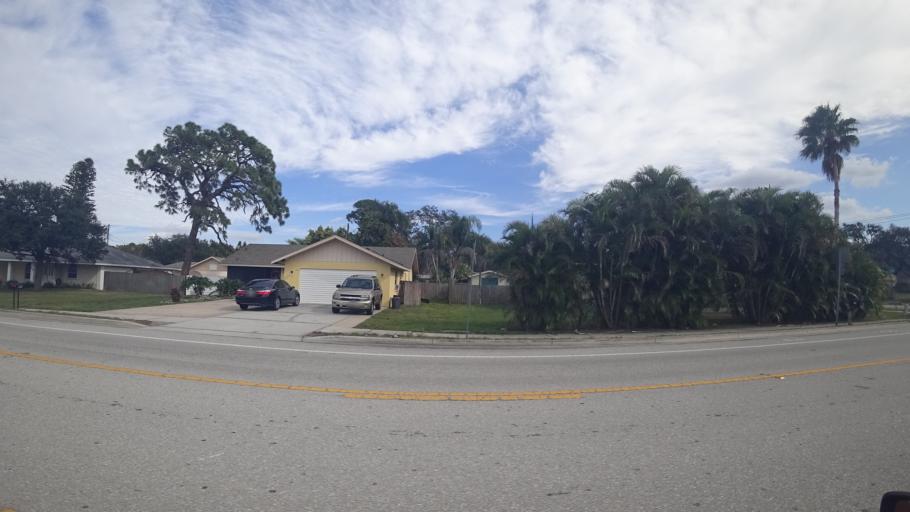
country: US
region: Florida
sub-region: Manatee County
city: West Bradenton
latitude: 27.5039
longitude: -82.6366
